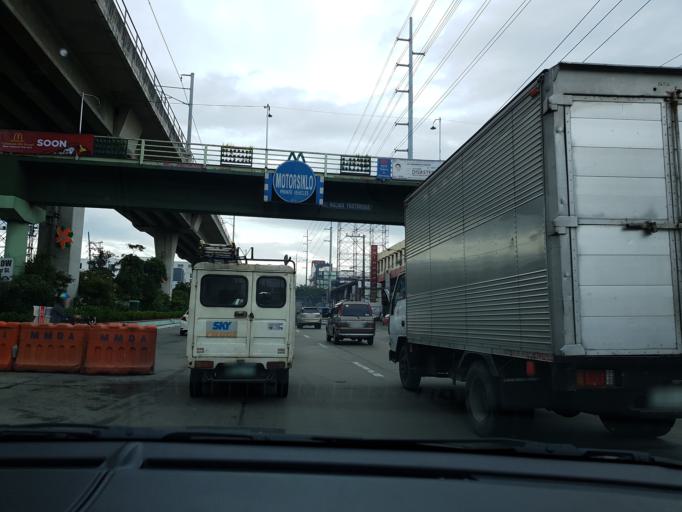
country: PH
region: Calabarzon
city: Del Monte
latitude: 14.6572
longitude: 120.9929
